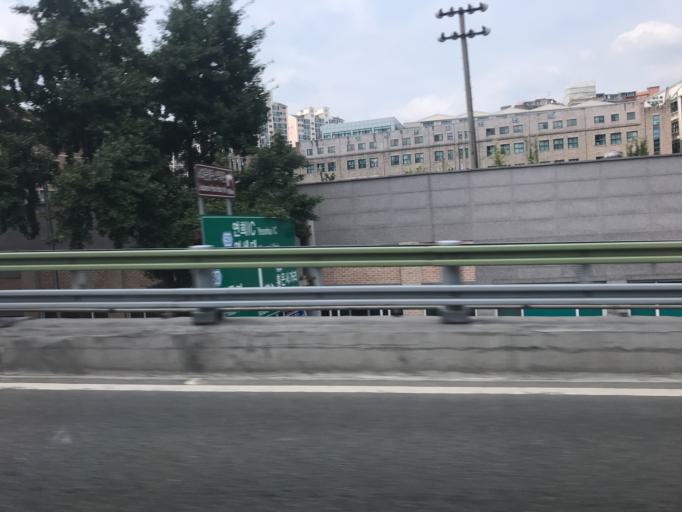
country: KR
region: Seoul
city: Seoul
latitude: 37.5725
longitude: 126.9622
